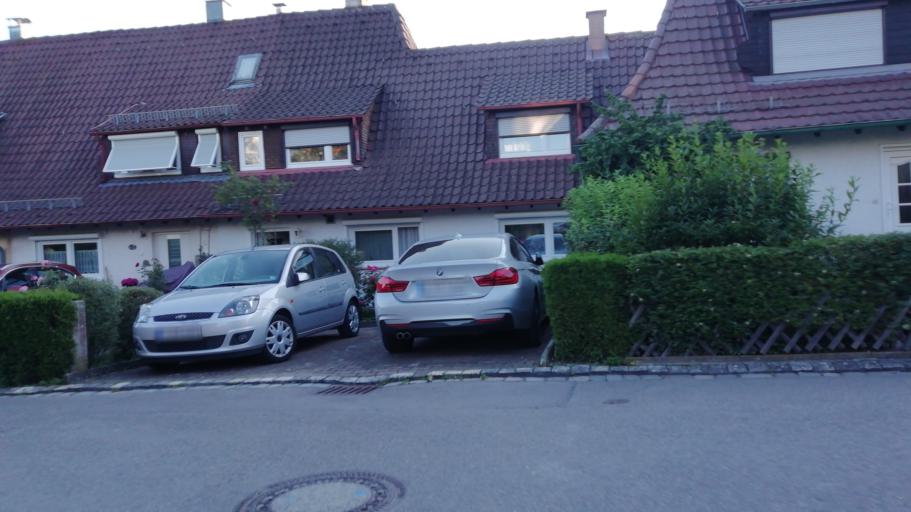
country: DE
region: Baden-Wuerttemberg
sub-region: Regierungsbezirk Stuttgart
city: Korntal
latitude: 48.8169
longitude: 9.1186
